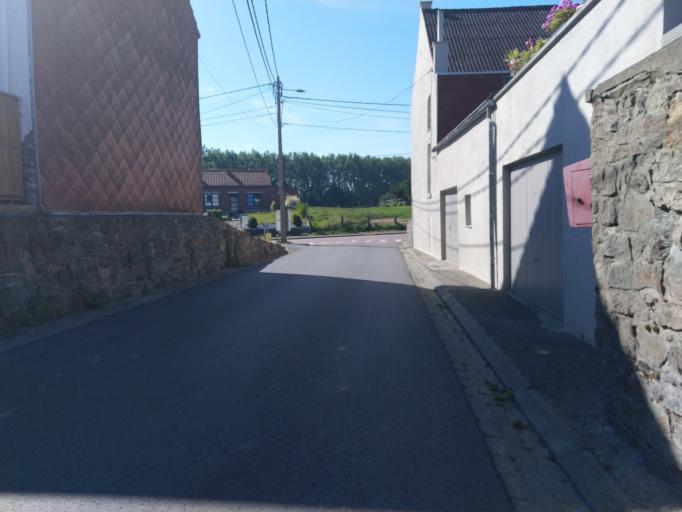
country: BE
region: Wallonia
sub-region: Province du Hainaut
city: Quevy-le-Petit
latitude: 50.3426
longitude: 3.9466
